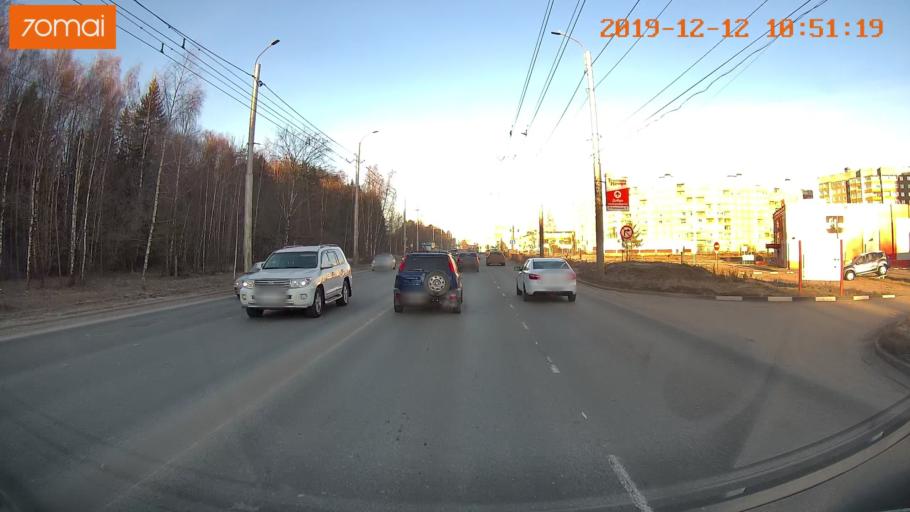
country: RU
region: Ivanovo
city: Kokhma
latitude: 56.9529
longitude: 41.0444
